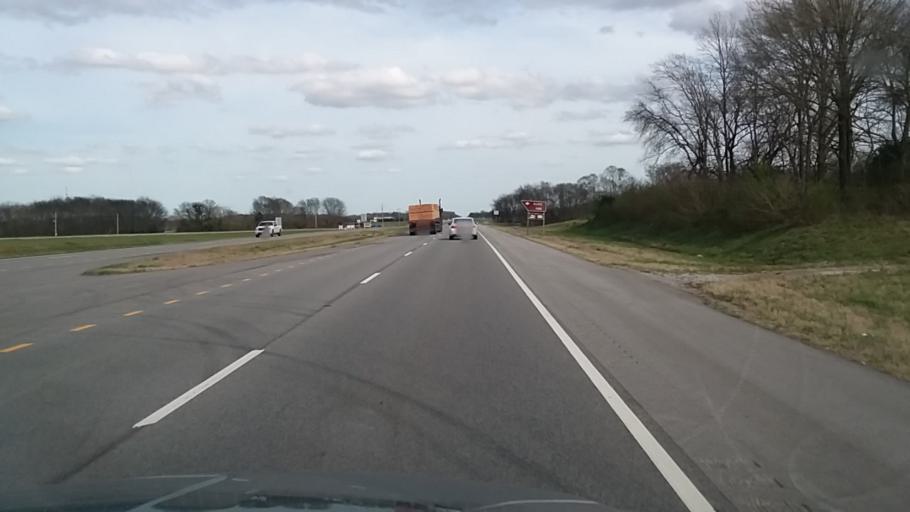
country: US
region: Alabama
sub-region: Lawrence County
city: Town Creek
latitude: 34.6839
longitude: -87.5328
